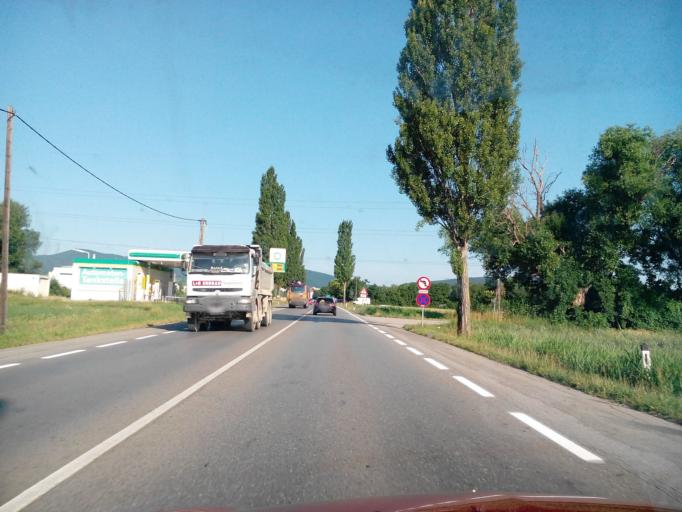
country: AT
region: Lower Austria
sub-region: Politischer Bezirk Baden
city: Pfaffstatten
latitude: 47.9926
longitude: 16.2700
